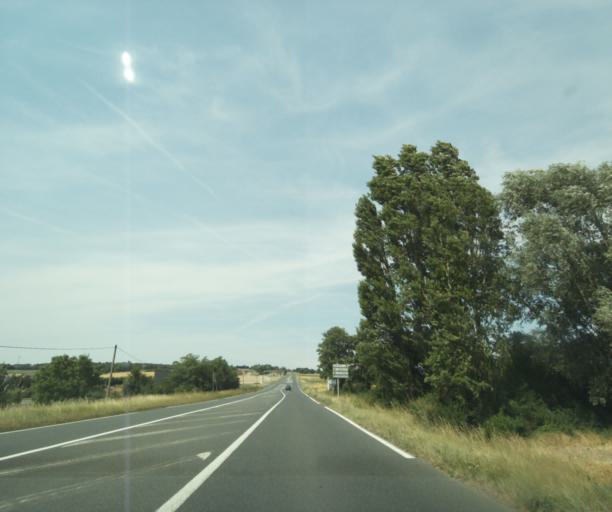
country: FR
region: Centre
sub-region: Departement d'Indre-et-Loire
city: La Celle-Saint-Avant
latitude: 47.0496
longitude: 0.6134
